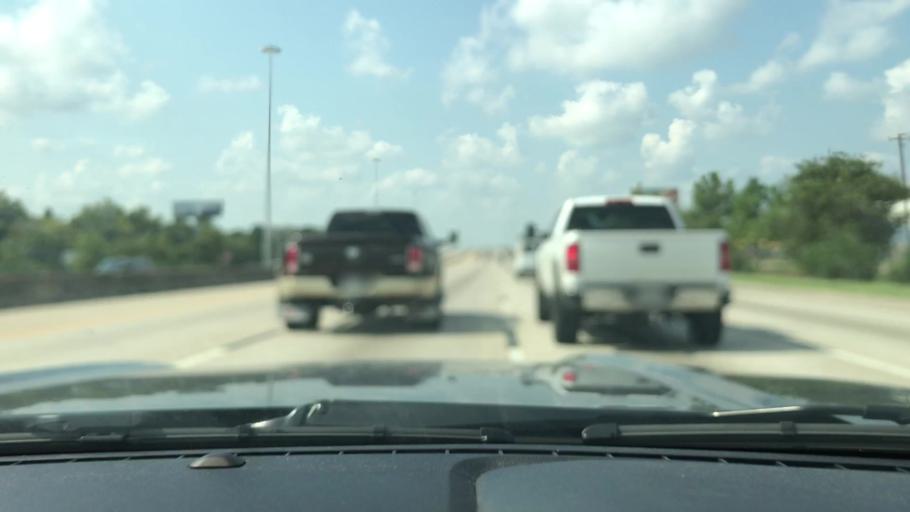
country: US
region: Texas
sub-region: Harris County
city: Aldine
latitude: 29.8845
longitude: -95.3223
